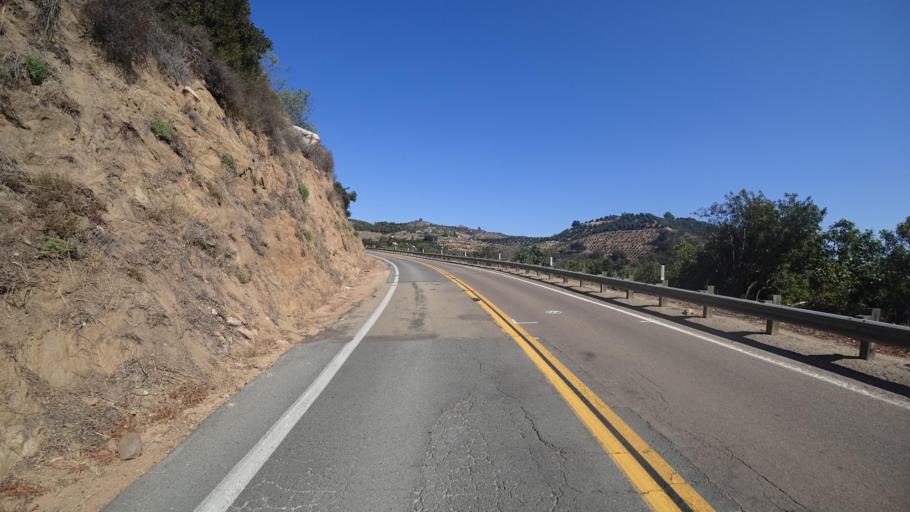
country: US
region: California
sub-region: San Diego County
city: Hidden Meadows
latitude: 33.2626
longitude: -117.1401
